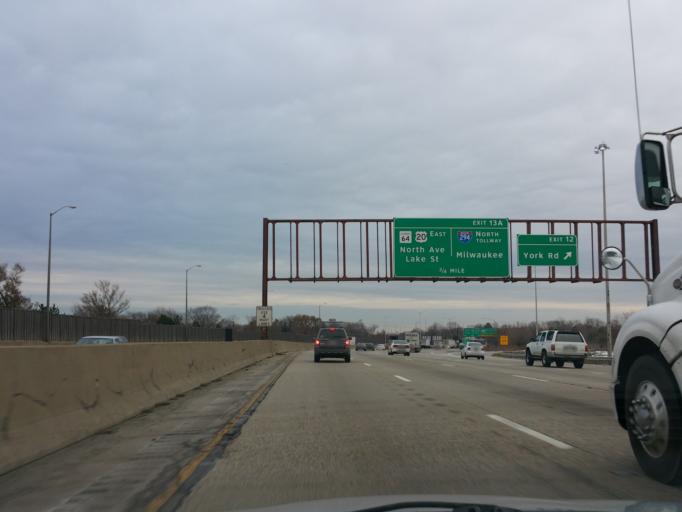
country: US
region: Illinois
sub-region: DuPage County
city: Elmhurst
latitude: 41.9120
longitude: -87.9359
